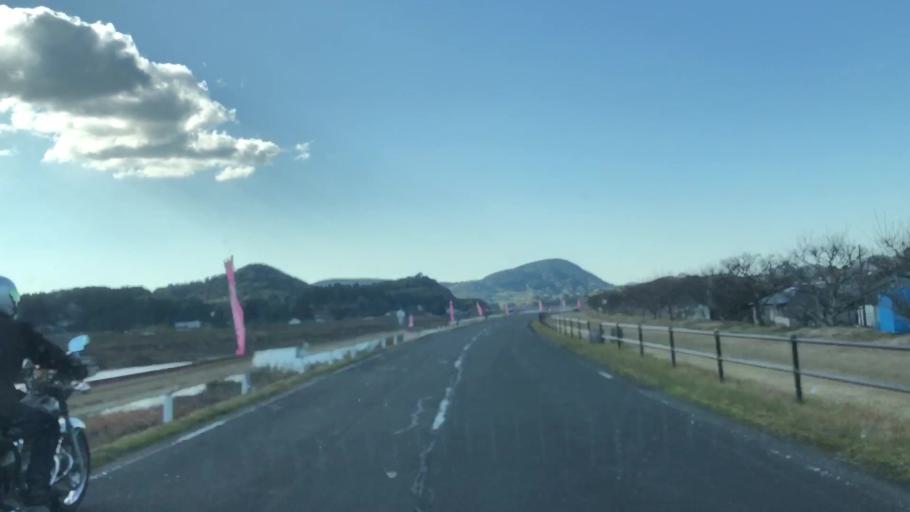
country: JP
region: Kagoshima
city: Satsumasendai
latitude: 31.8593
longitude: 130.3472
